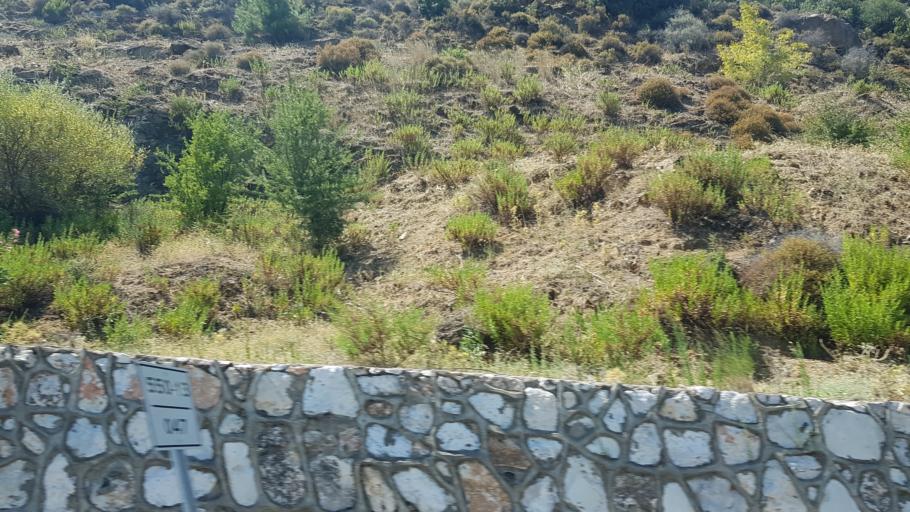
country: TR
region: Aydin
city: Akcaova
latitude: 37.5117
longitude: 28.0973
